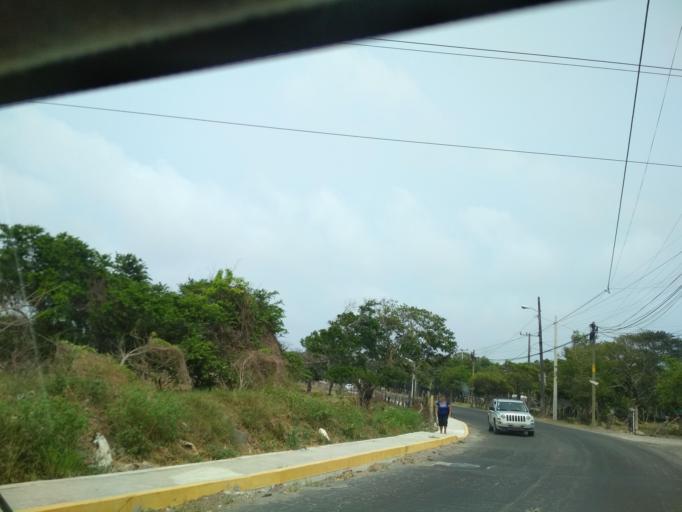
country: MX
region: Veracruz
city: Boca del Rio
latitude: 19.0949
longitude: -96.1202
